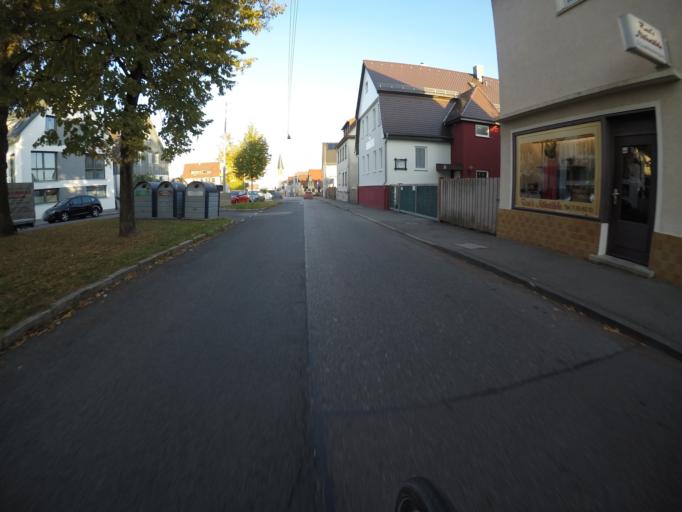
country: DE
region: Baden-Wuerttemberg
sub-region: Regierungsbezirk Stuttgart
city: Gerlingen
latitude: 48.7397
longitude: 9.1011
